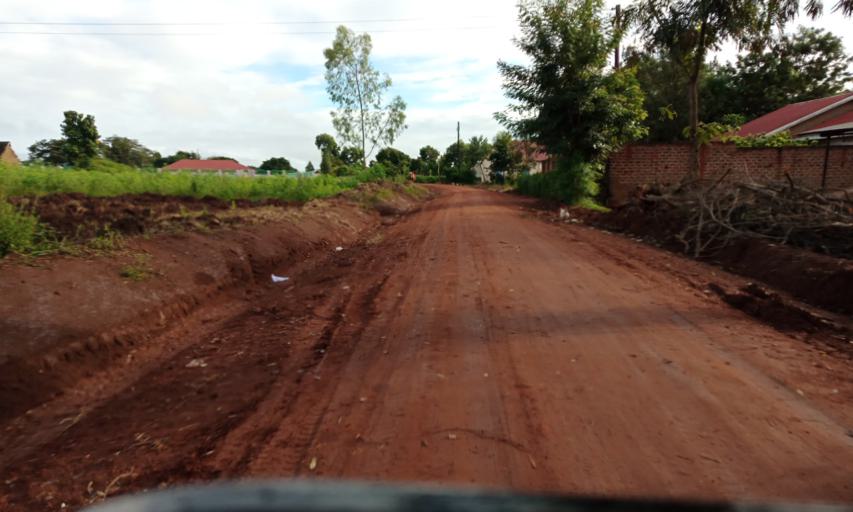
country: UG
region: Eastern Region
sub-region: Mbale District
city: Mbale
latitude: 1.1403
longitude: 34.1689
